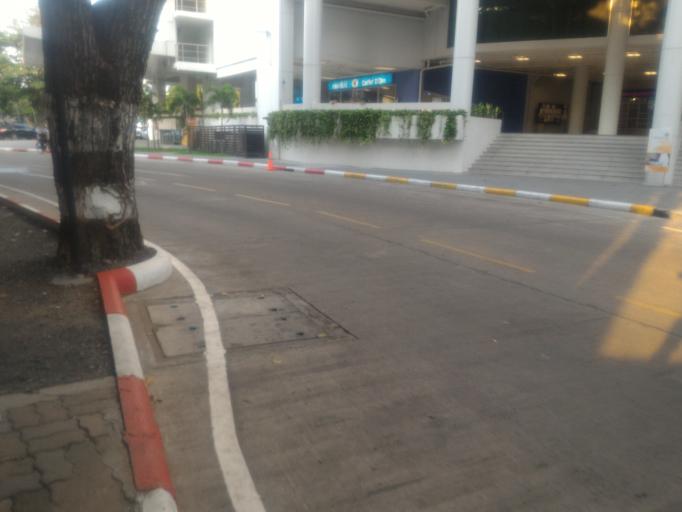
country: TH
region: Bangkok
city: Thung Khru
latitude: 13.6502
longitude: 100.4952
